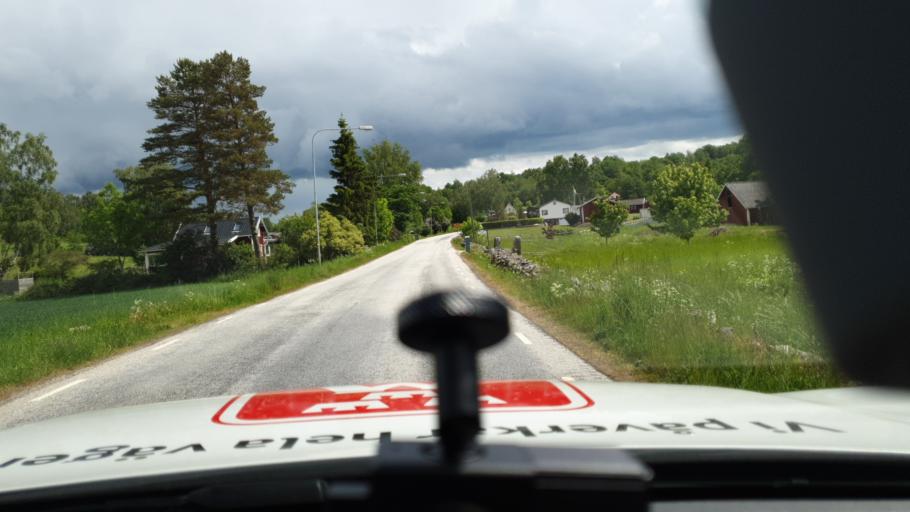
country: SE
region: Vaestra Goetaland
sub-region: Skovde Kommun
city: Stopen
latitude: 58.5246
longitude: 13.7696
